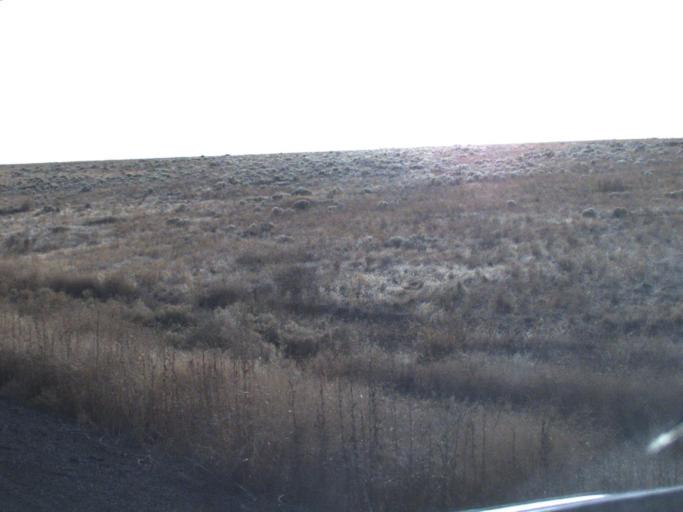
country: US
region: Washington
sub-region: Adams County
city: Ritzville
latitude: 47.1832
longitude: -118.6876
